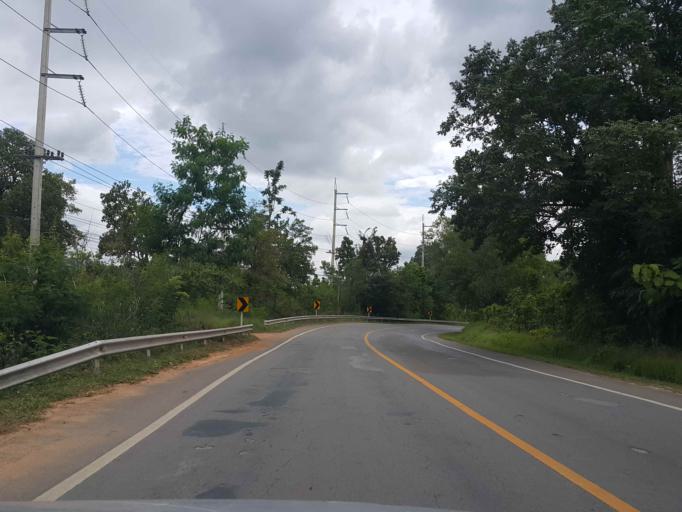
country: TH
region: Lamphun
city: Thung Hua Chang
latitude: 17.9742
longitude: 98.8777
